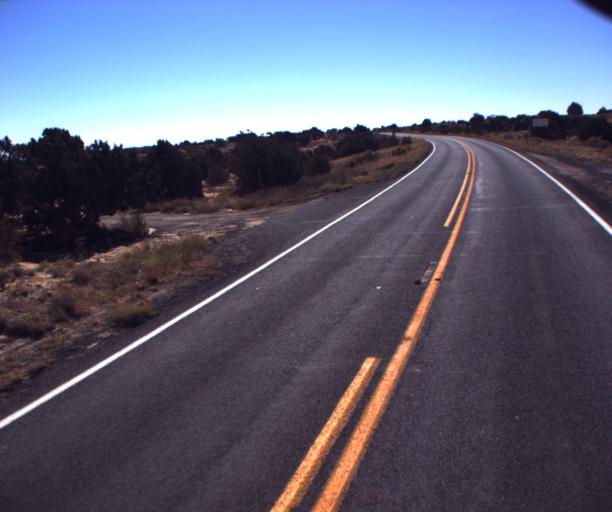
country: US
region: Arizona
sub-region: Navajo County
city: First Mesa
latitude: 35.9069
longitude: -110.6666
